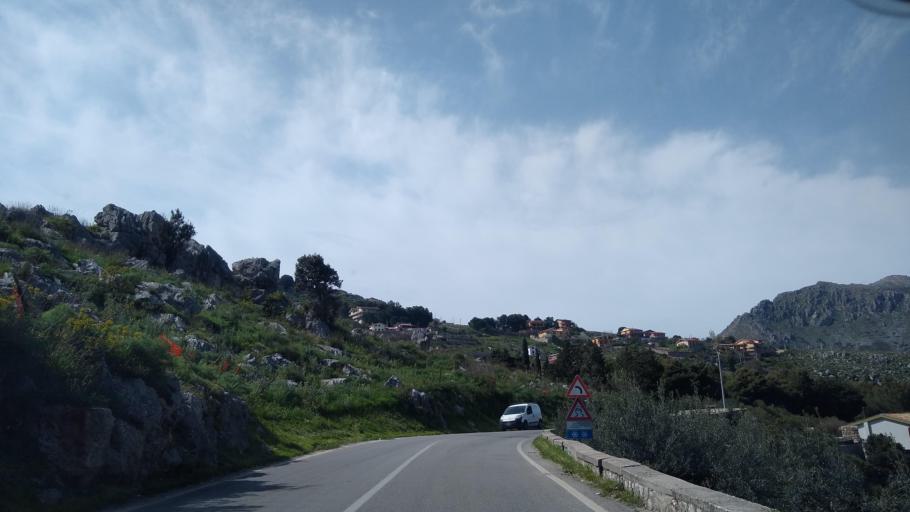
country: IT
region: Sicily
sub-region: Palermo
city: Giacalone
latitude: 38.0365
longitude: 13.2177
